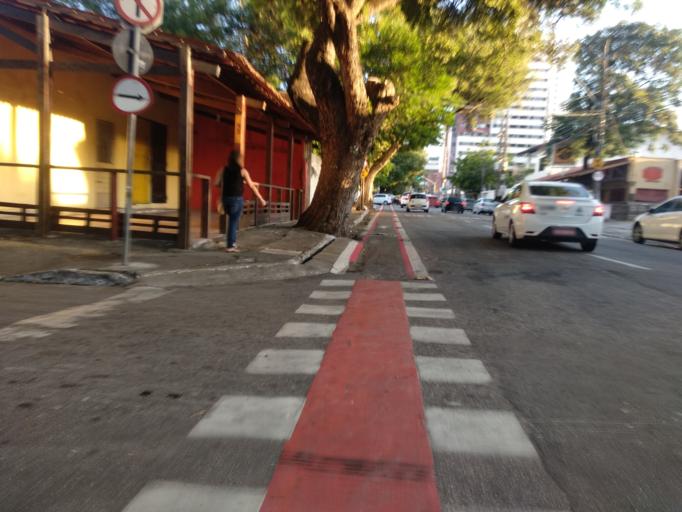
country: BR
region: Ceara
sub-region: Fortaleza
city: Fortaleza
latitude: -3.7340
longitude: -38.5087
